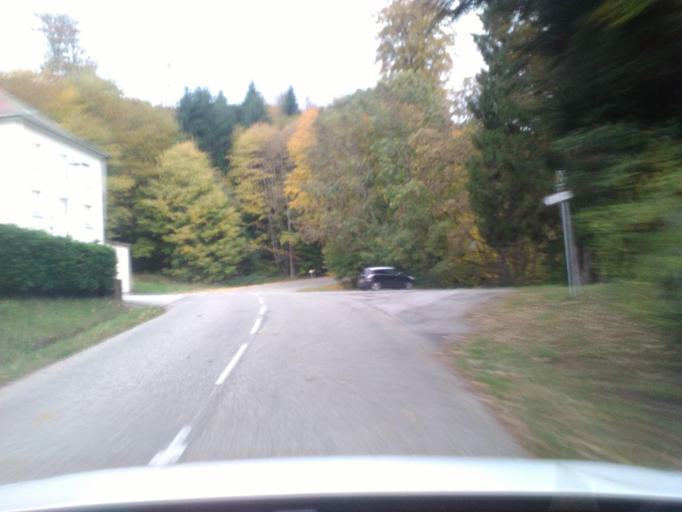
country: FR
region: Lorraine
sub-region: Departement des Vosges
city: Ban-de-Laveline
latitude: 48.3622
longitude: 7.1052
